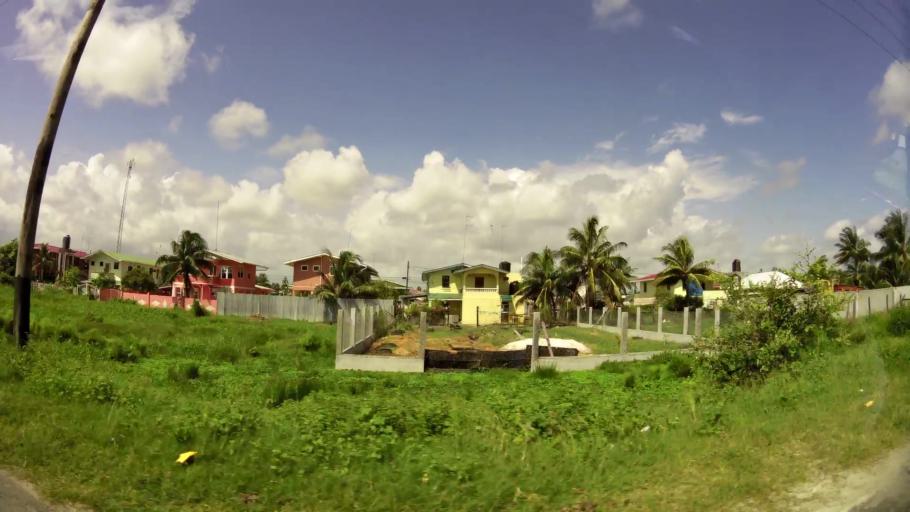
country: GY
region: Demerara-Mahaica
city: Mahaica Village
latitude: 6.7714
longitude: -58.0055
